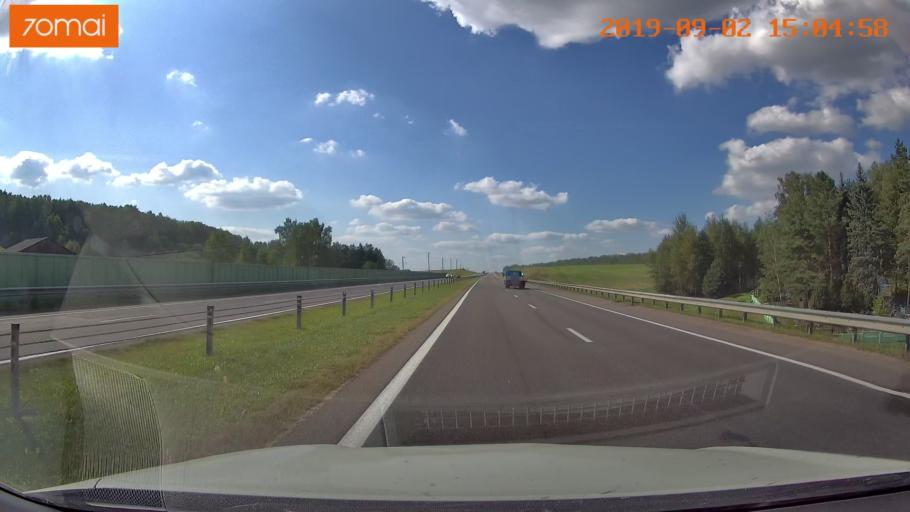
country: BY
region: Mogilev
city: Vishow
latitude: 53.9785
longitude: 29.9426
